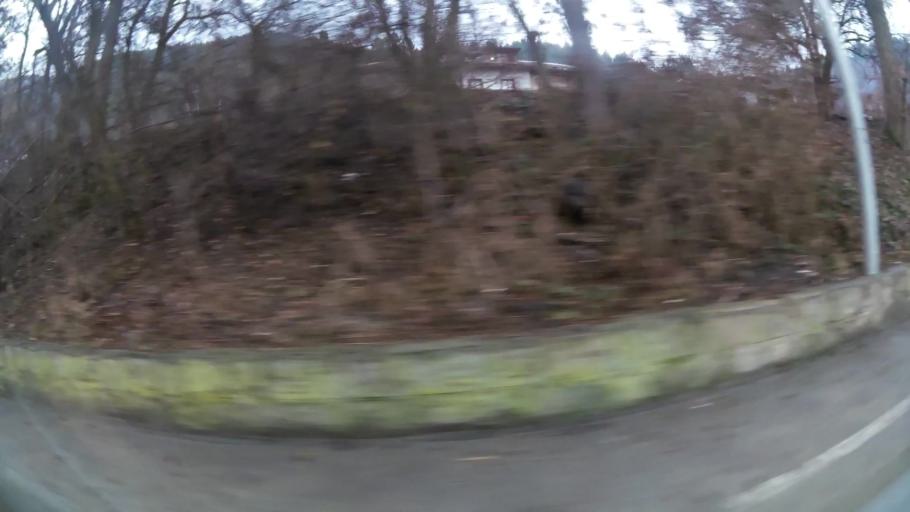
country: BG
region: Sofia-Capital
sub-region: Stolichna Obshtina
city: Sofia
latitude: 42.5824
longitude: 23.4281
